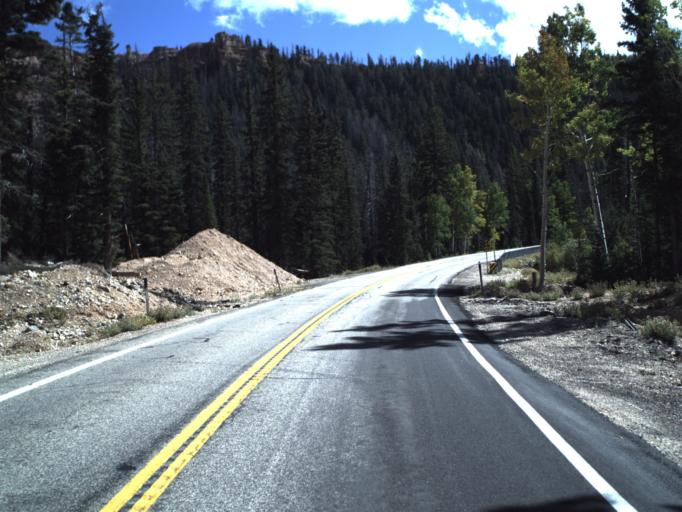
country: US
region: Utah
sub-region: Iron County
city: Cedar City
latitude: 37.5913
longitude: -112.8820
